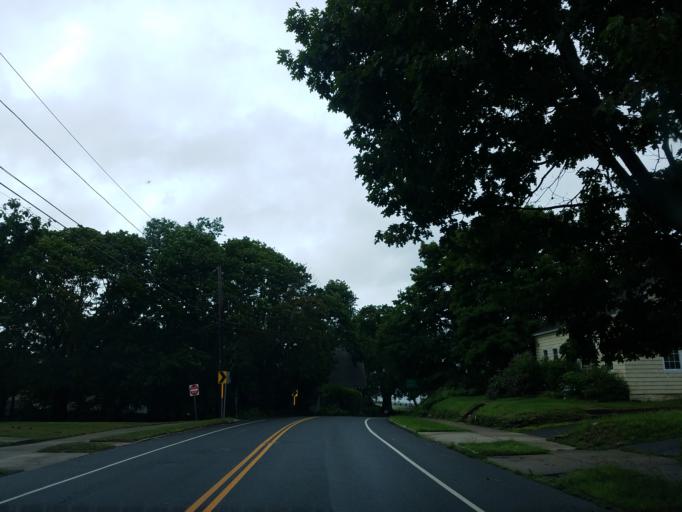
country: US
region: Connecticut
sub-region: New Haven County
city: East Haven
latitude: 41.2659
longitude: -72.8965
